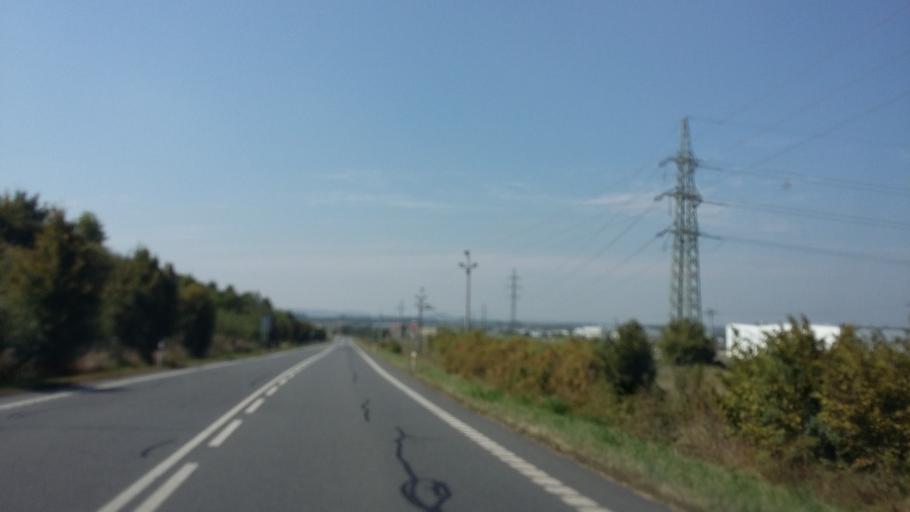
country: CZ
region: Central Bohemia
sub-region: Okres Kolin
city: Kolin
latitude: 50.0667
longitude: 15.2406
